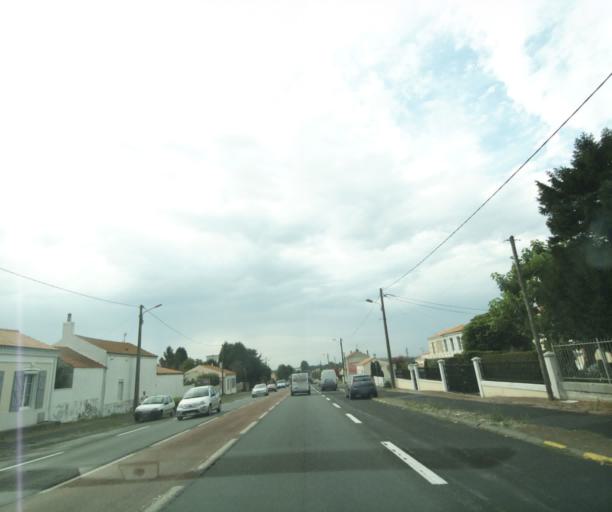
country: FR
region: Poitou-Charentes
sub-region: Departement de la Charente-Maritime
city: Tonnay-Charente
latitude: 45.9489
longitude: -0.9174
